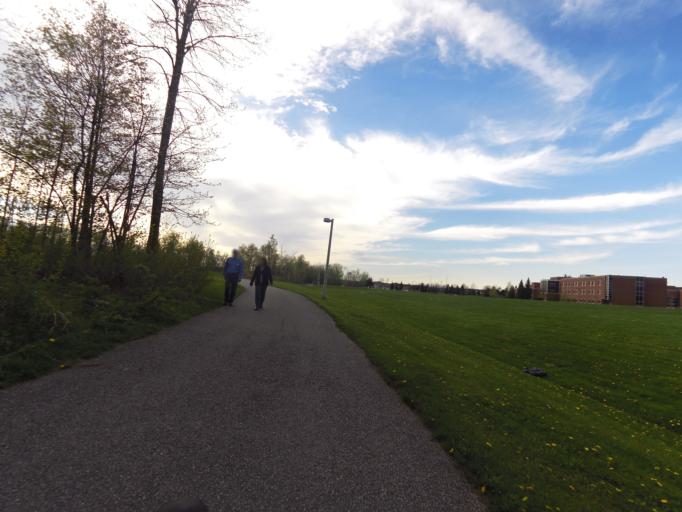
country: CA
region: Ontario
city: Bells Corners
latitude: 45.2827
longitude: -75.7396
